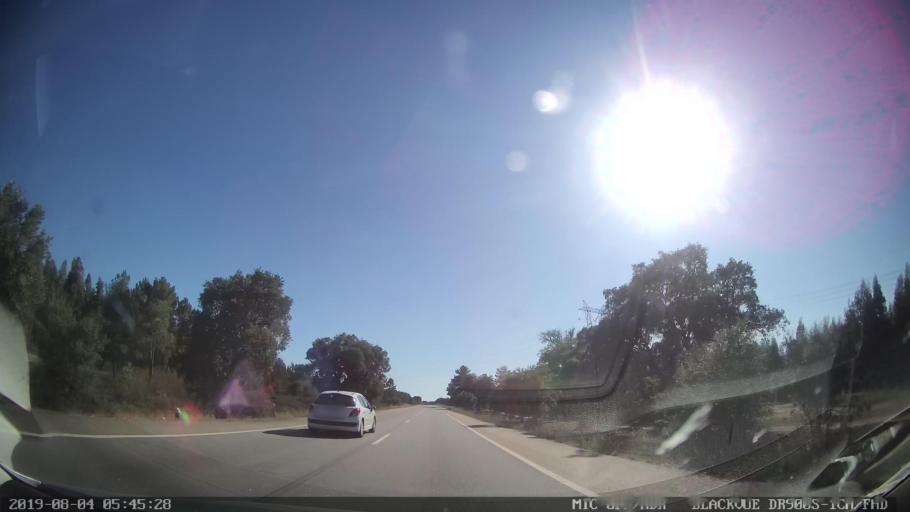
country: PT
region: Portalegre
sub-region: Nisa
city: Nisa
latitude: 39.4623
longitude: -7.7739
